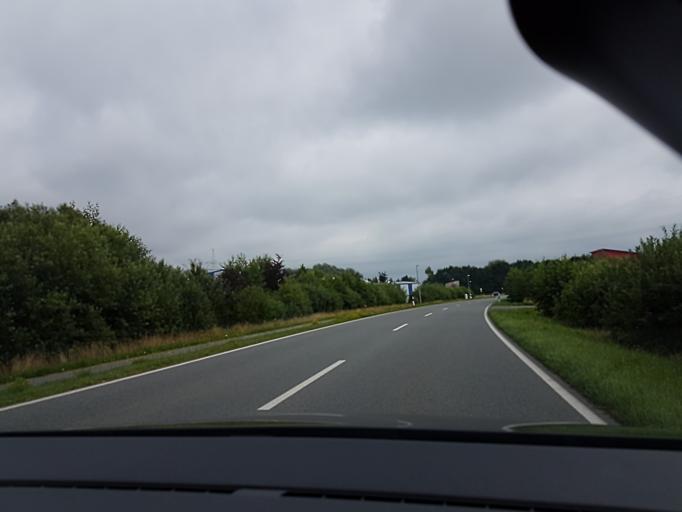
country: DE
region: Lower Saxony
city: Stuhr
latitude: 53.0237
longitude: 8.6884
